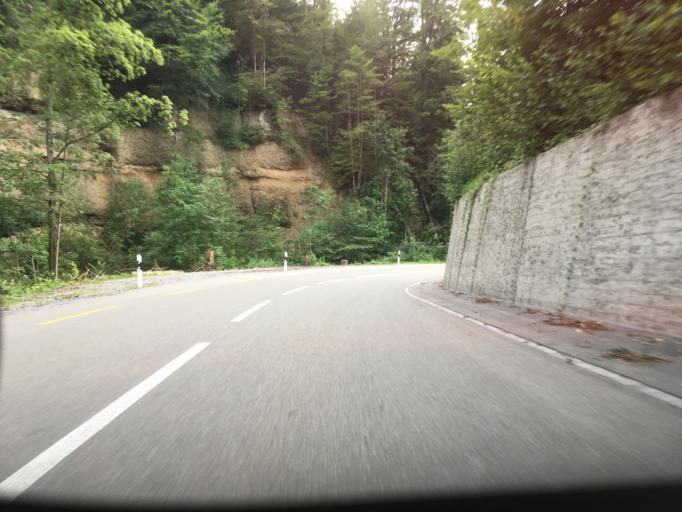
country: CH
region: Zurich
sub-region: Bezirk Pfaeffikon
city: Bauma
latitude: 47.3500
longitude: 8.9438
